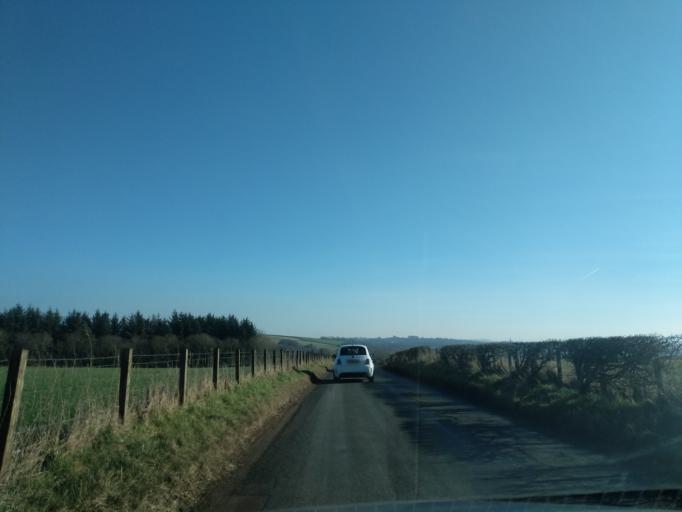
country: GB
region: Scotland
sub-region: South Lanarkshire
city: Lanark
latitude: 55.6868
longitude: -3.8264
